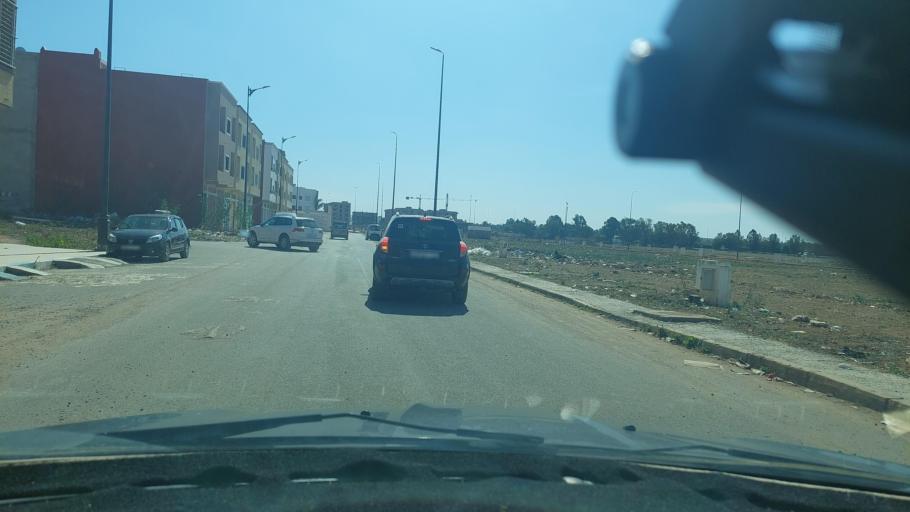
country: MA
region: Grand Casablanca
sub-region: Mediouna
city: Mediouna
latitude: 33.3804
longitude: -7.5374
